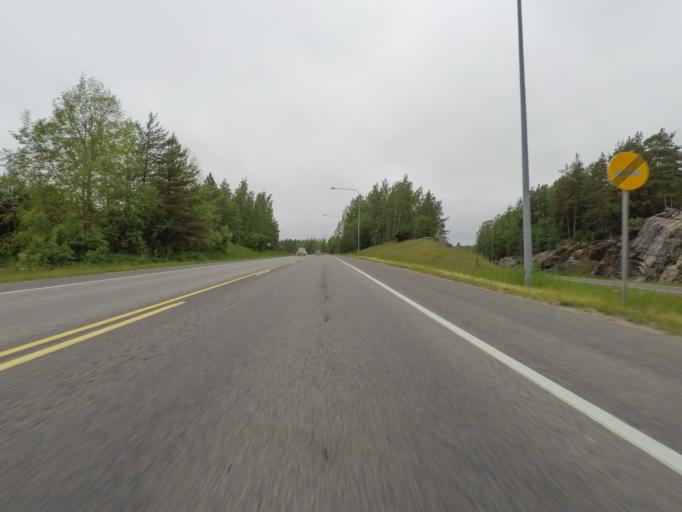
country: FI
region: Varsinais-Suomi
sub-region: Turku
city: Raisio
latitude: 60.4610
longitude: 22.1765
